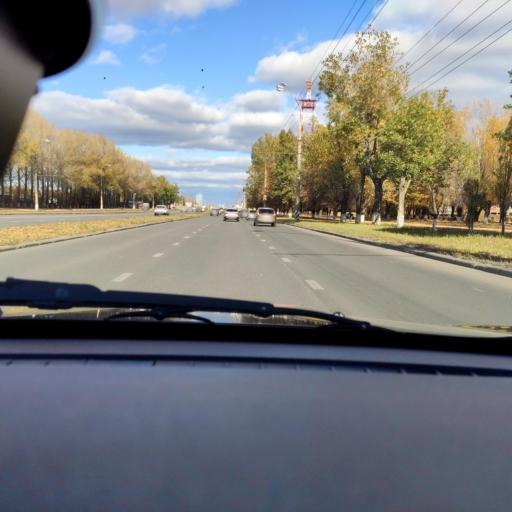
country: RU
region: Samara
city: Tol'yatti
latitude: 53.5259
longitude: 49.2607
